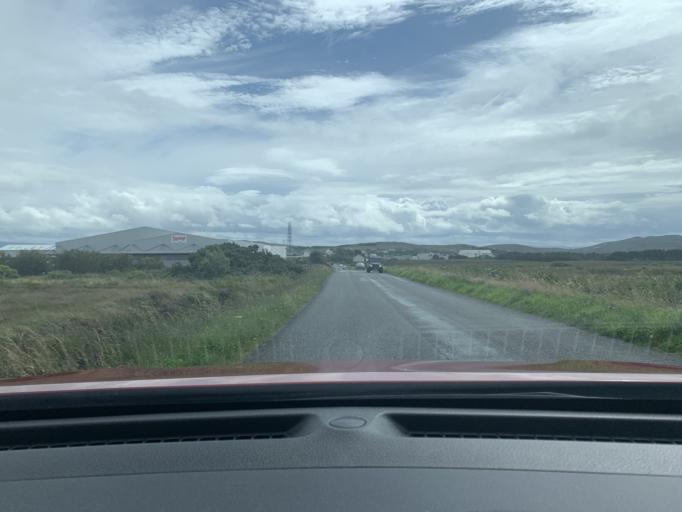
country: IE
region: Ulster
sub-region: County Donegal
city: Dungloe
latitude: 54.9599
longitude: -8.3655
